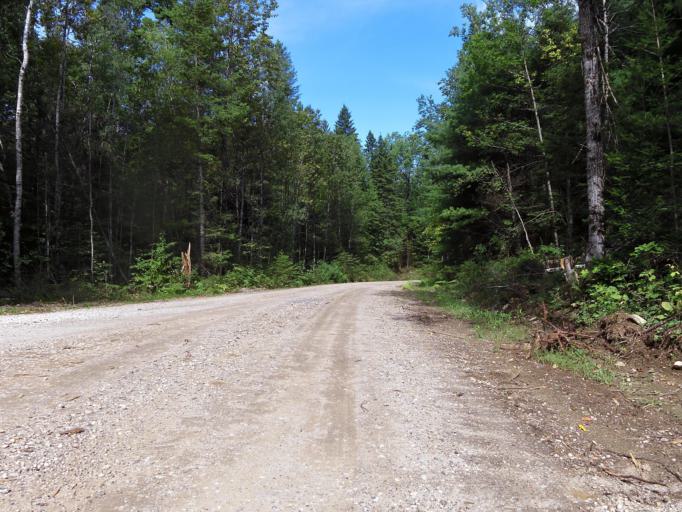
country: CA
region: Ontario
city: Renfrew
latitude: 45.1148
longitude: -76.7260
